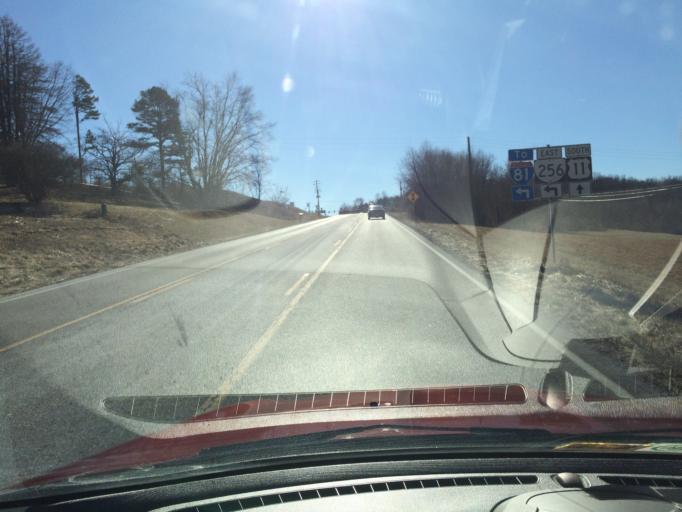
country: US
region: Virginia
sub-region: Augusta County
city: Weyers Cave
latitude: 38.2924
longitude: -78.9354
